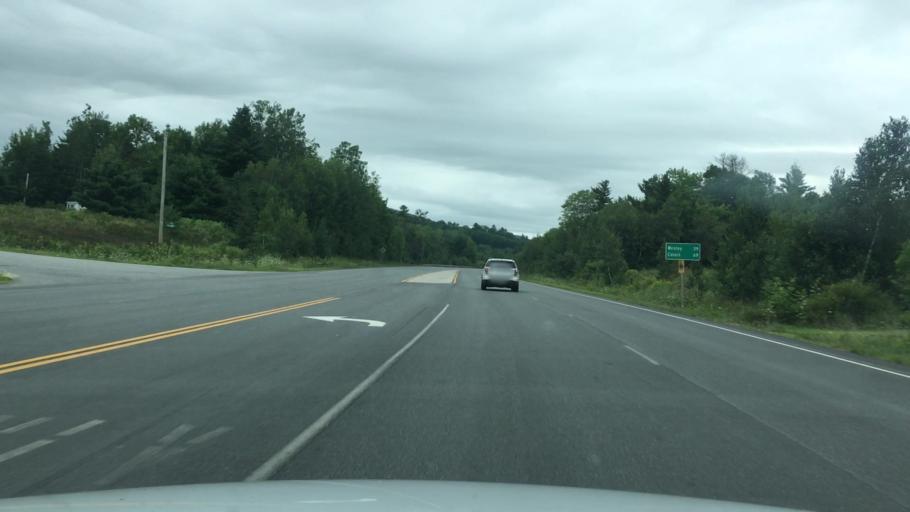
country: US
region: Maine
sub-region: Hancock County
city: Franklin
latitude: 44.8514
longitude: -68.3293
